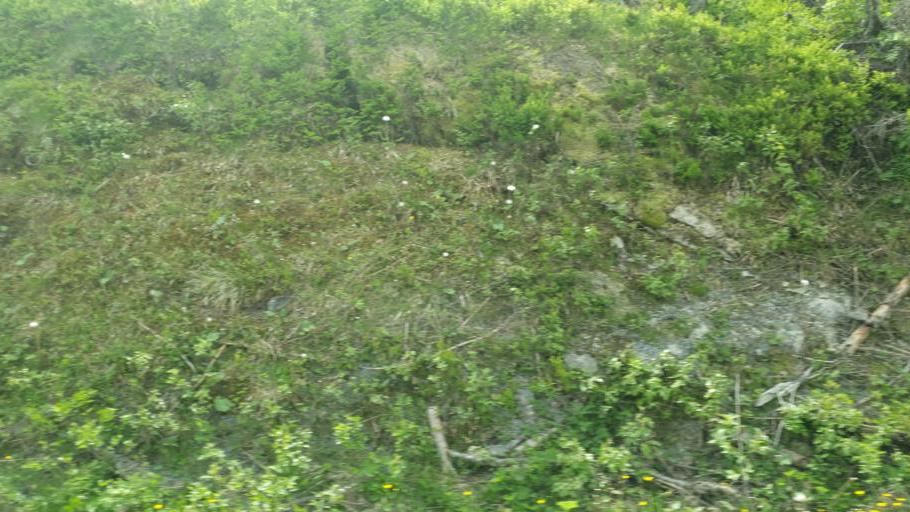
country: NO
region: Nord-Trondelag
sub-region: Leksvik
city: Leksvik
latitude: 63.6896
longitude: 10.5261
